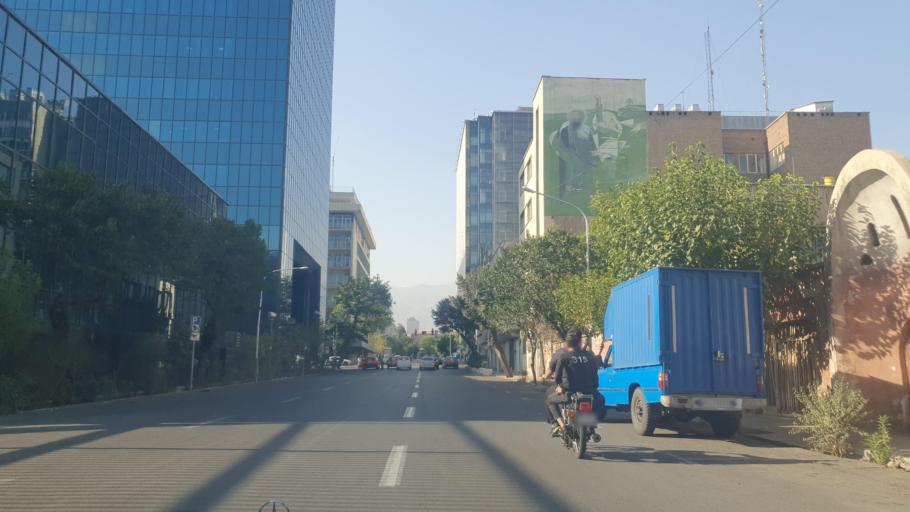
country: IR
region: Tehran
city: Tehran
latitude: 35.7058
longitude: 51.4211
